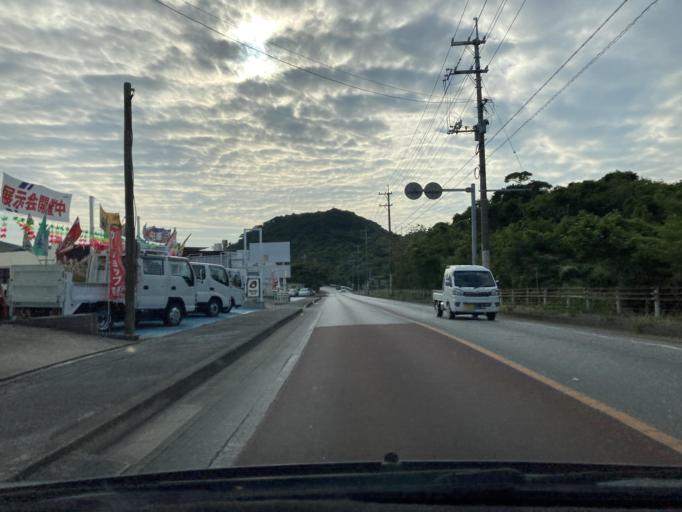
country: JP
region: Okinawa
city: Okinawa
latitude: 26.3702
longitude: 127.8130
